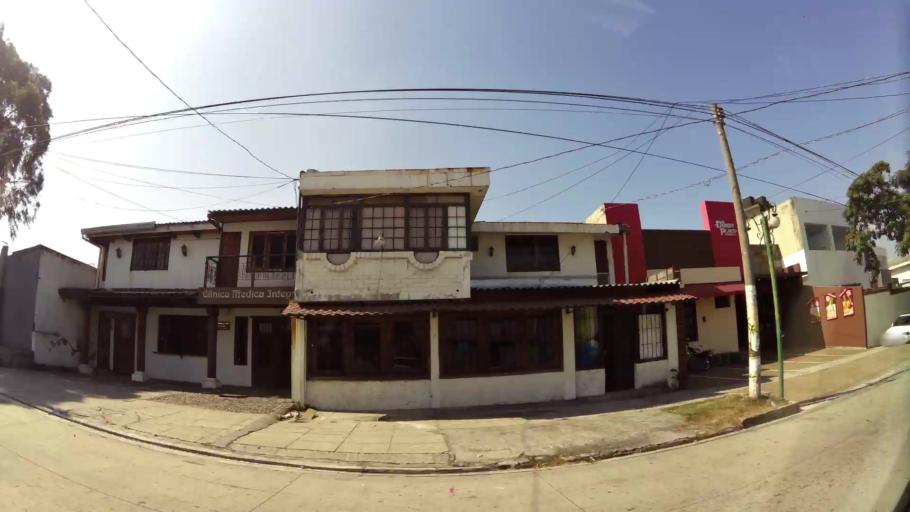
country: SV
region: La Libertad
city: Antiguo Cuscatlan
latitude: 13.6756
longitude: -89.2444
